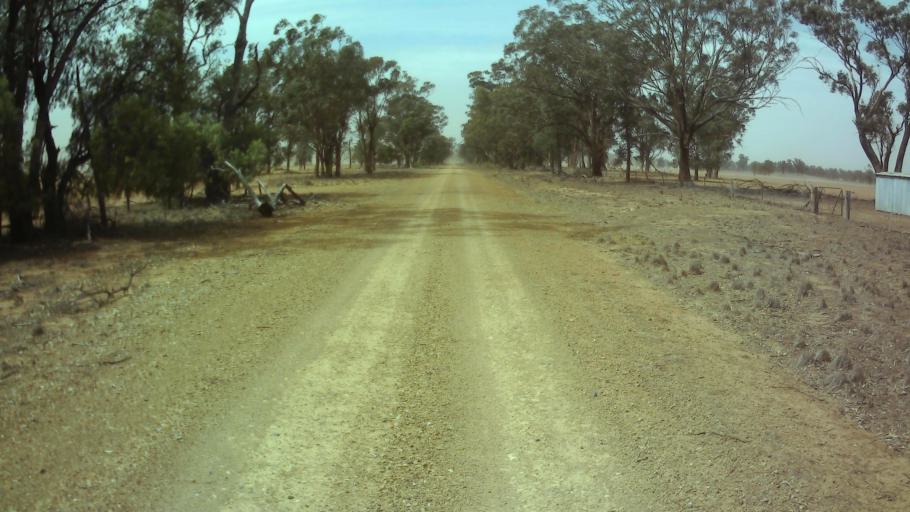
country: AU
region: New South Wales
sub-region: Weddin
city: Grenfell
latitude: -33.7315
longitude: 147.9627
